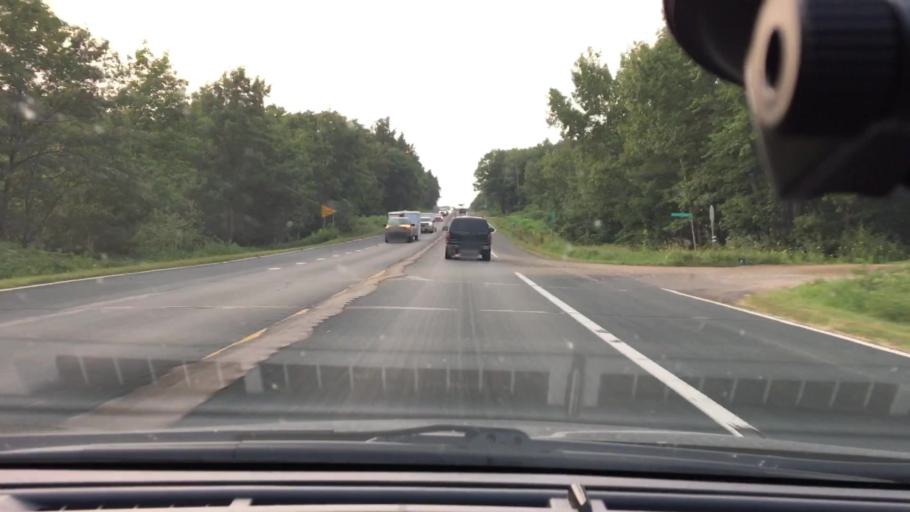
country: US
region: Minnesota
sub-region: Mille Lacs County
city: Vineland
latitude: 46.2439
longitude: -93.8086
